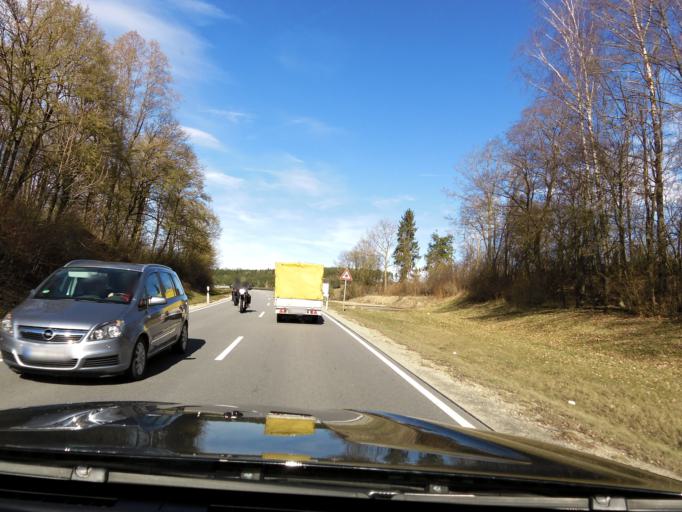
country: DE
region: Bavaria
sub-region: Lower Bavaria
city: Essenbach
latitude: 48.6223
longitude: 12.2184
